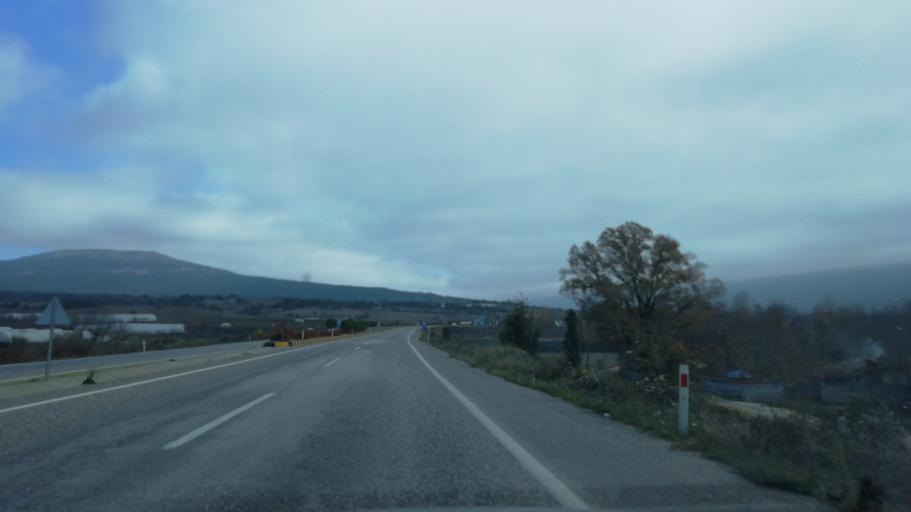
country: TR
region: Karabuk
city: Safranbolu
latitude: 41.2231
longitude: 32.7777
